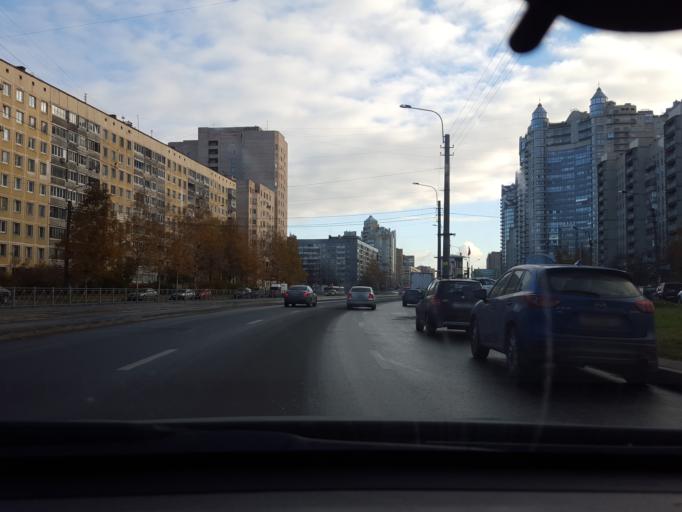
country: RU
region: St.-Petersburg
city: Ozerki
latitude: 60.0446
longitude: 30.3239
